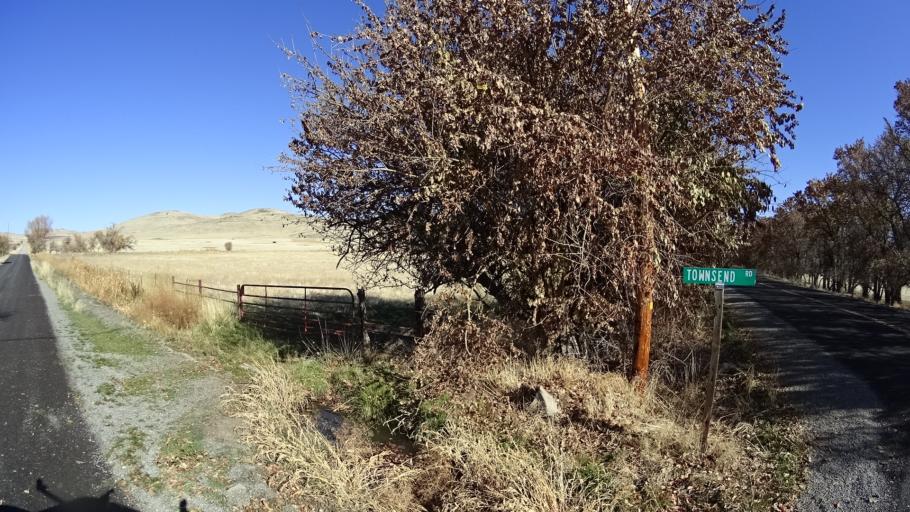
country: US
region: California
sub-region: Siskiyou County
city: Montague
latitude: 41.7264
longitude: -122.3988
